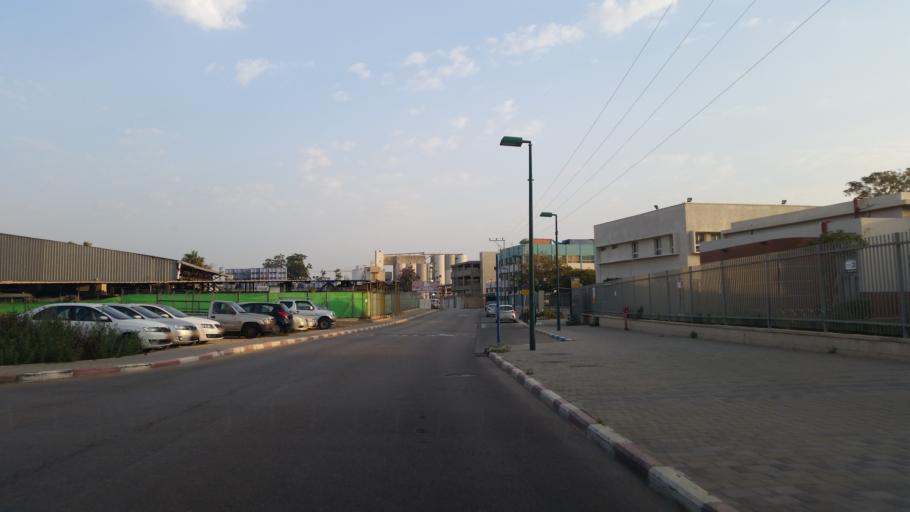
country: IL
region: Central District
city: Netanya
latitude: 32.3160
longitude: 34.8714
